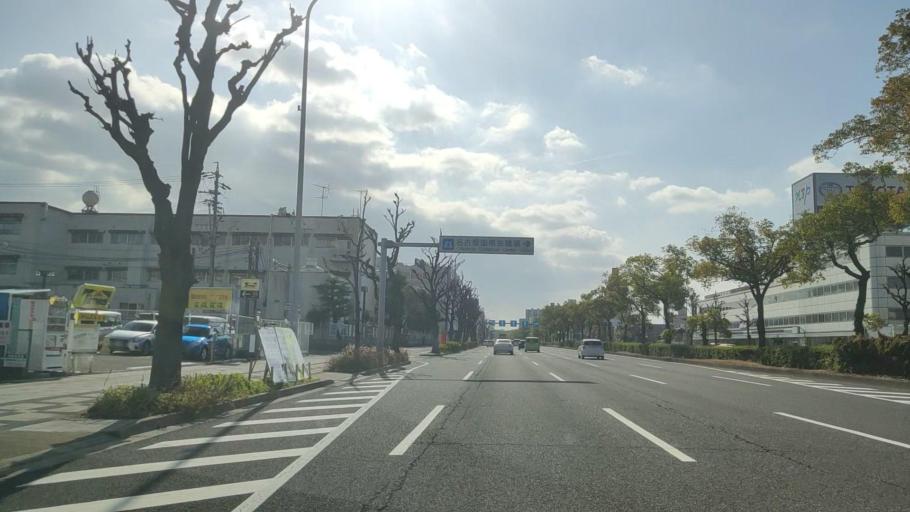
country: JP
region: Aichi
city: Nagoya-shi
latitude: 35.1368
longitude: 136.9004
